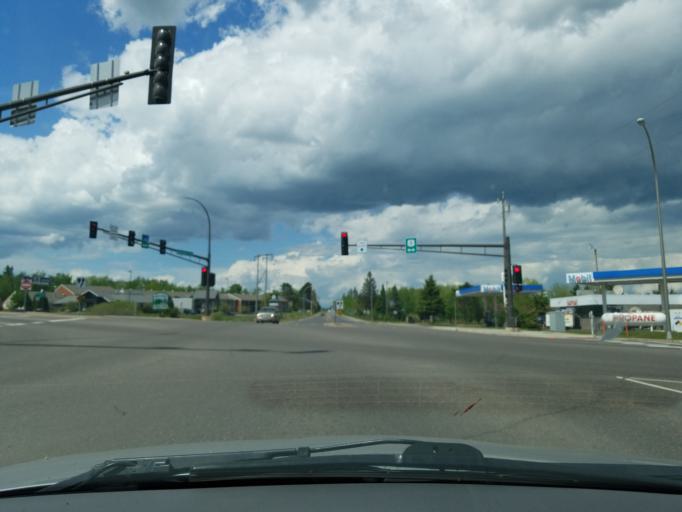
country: US
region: Minnesota
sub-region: Saint Louis County
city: Proctor
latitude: 46.7379
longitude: -92.2171
